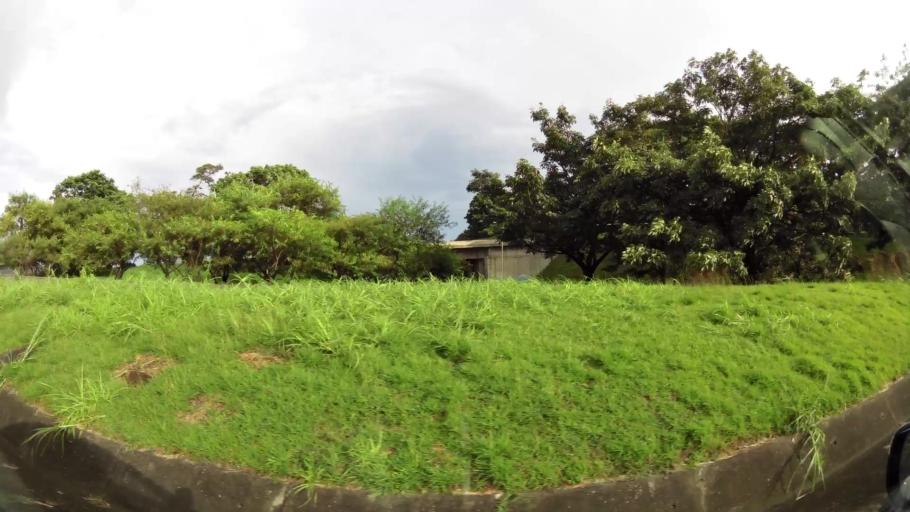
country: CR
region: San Jose
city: Colima
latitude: 9.9452
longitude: -84.1084
